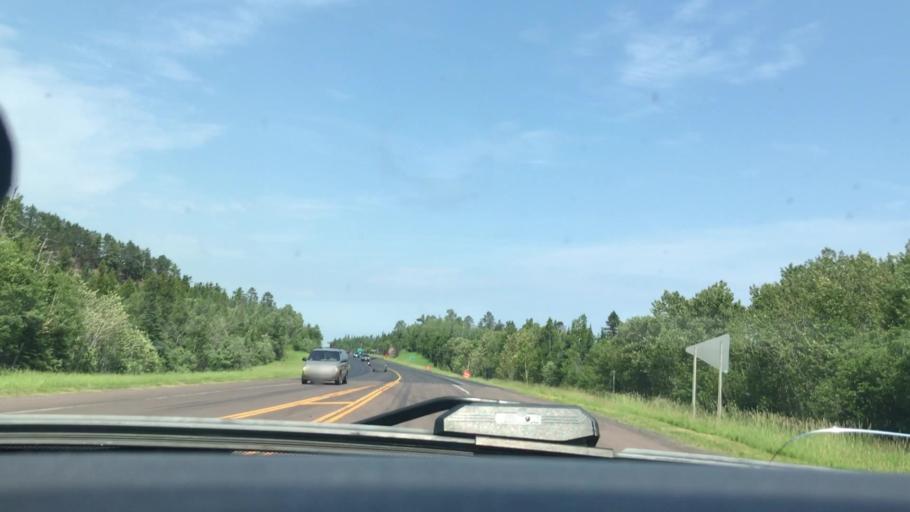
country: US
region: Minnesota
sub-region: Lake County
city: Silver Bay
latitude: 47.3417
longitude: -91.1935
